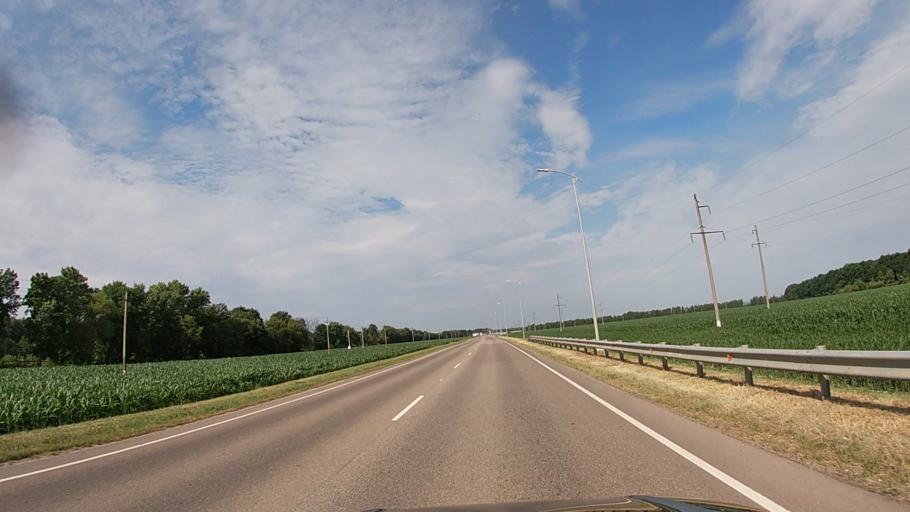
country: RU
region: Belgorod
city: Proletarskiy
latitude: 50.8008
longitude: 35.7276
